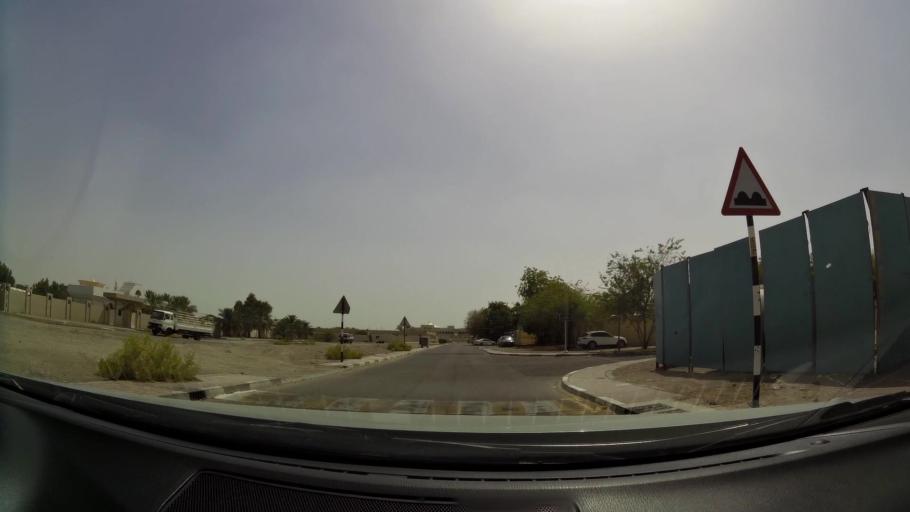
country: AE
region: Abu Dhabi
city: Al Ain
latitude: 24.2247
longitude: 55.6935
